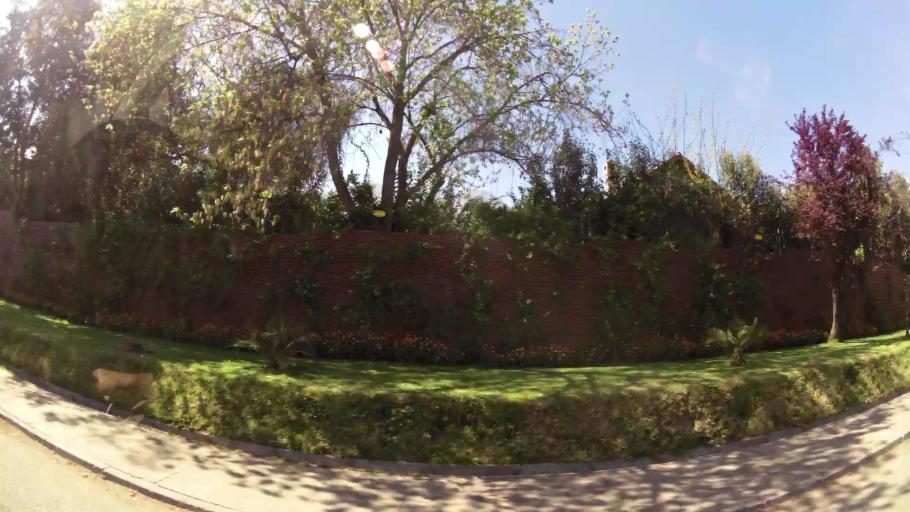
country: CL
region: Santiago Metropolitan
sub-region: Provincia de Santiago
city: Villa Presidente Frei, Nunoa, Santiago, Chile
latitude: -33.4503
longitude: -70.5200
